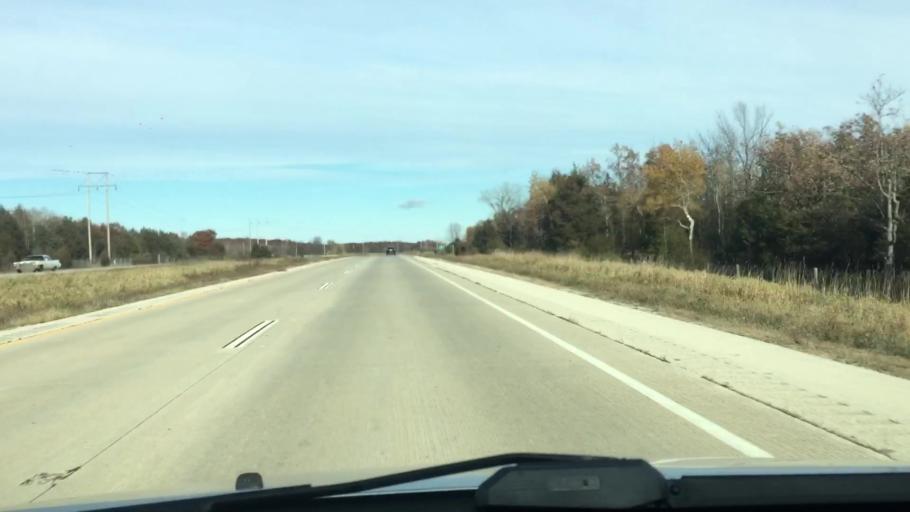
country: US
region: Wisconsin
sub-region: Kewaunee County
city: Luxemburg
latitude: 44.6274
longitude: -87.8153
